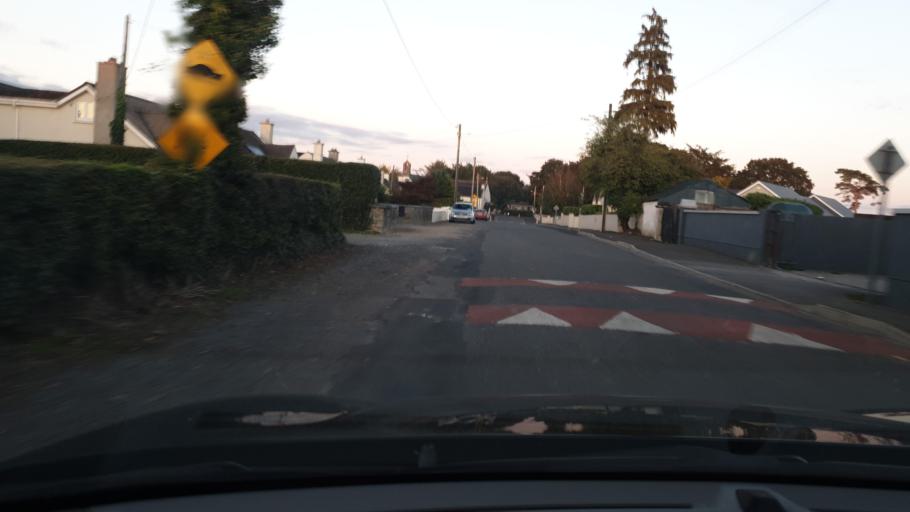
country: IE
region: Leinster
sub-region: Kildare
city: Prosperous
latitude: 53.3299
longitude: -6.7684
